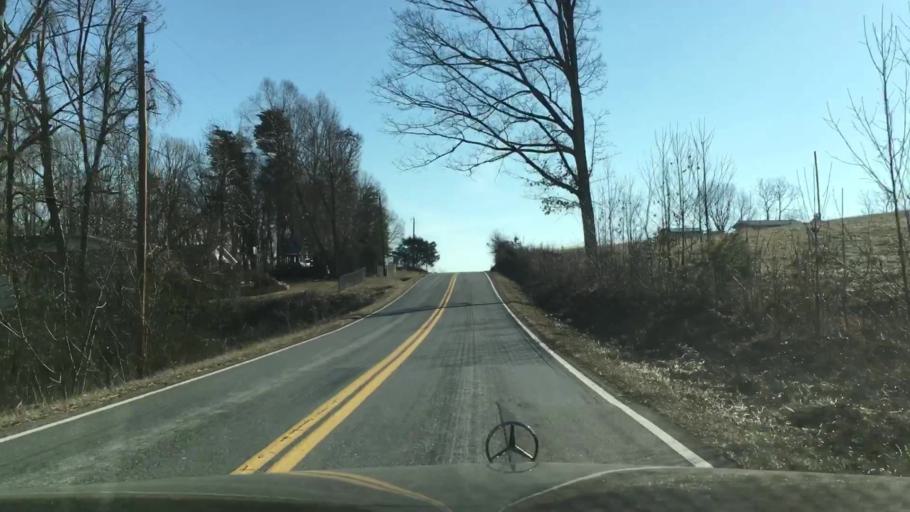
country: US
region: Virginia
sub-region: Campbell County
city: Altavista
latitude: 37.1535
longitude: -79.3455
